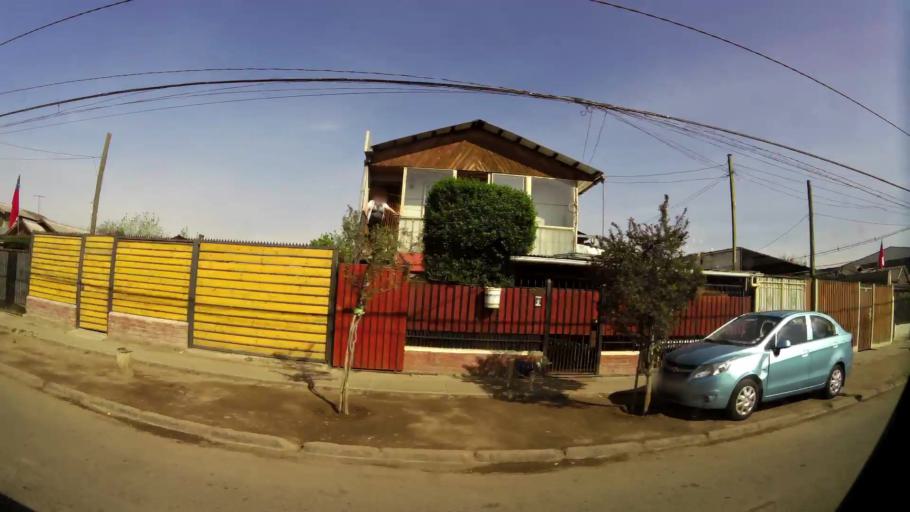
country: CL
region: Santiago Metropolitan
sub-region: Provincia de Santiago
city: Lo Prado
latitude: -33.4153
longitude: -70.7450
